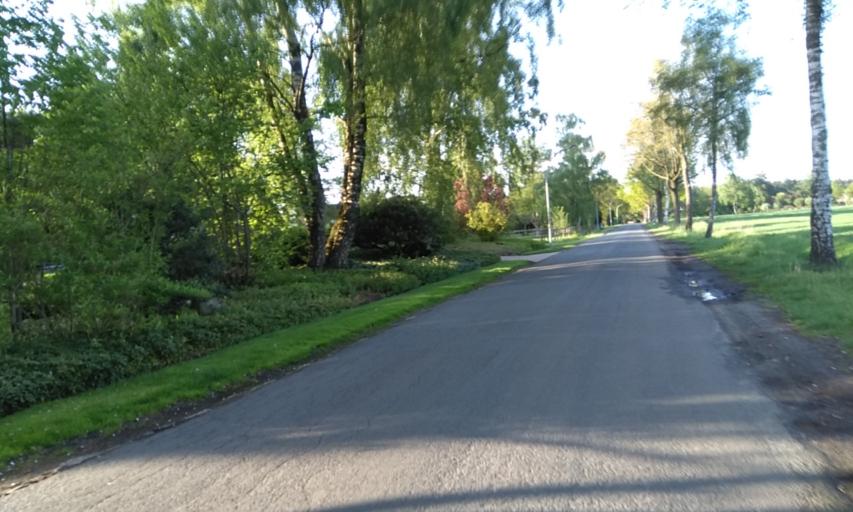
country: DE
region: Lower Saxony
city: Wohnste
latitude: 53.3912
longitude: 9.5041
